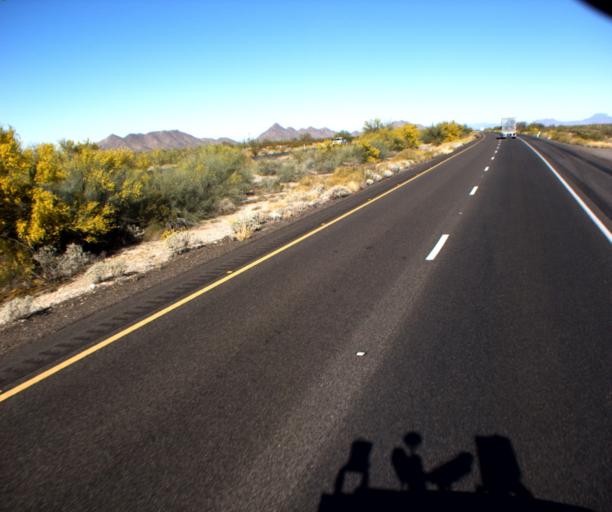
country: US
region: Arizona
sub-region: Maricopa County
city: Gila Bend
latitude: 32.8771
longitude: -112.4489
